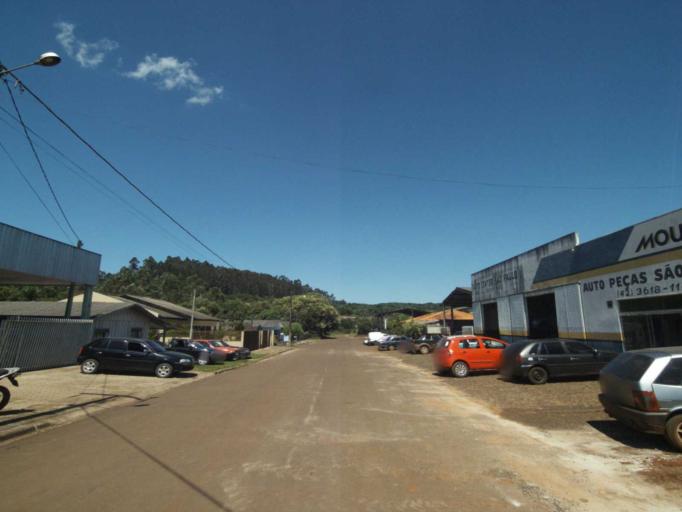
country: BR
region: Parana
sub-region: Laranjeiras Do Sul
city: Laranjeiras do Sul
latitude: -25.3793
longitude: -52.2012
